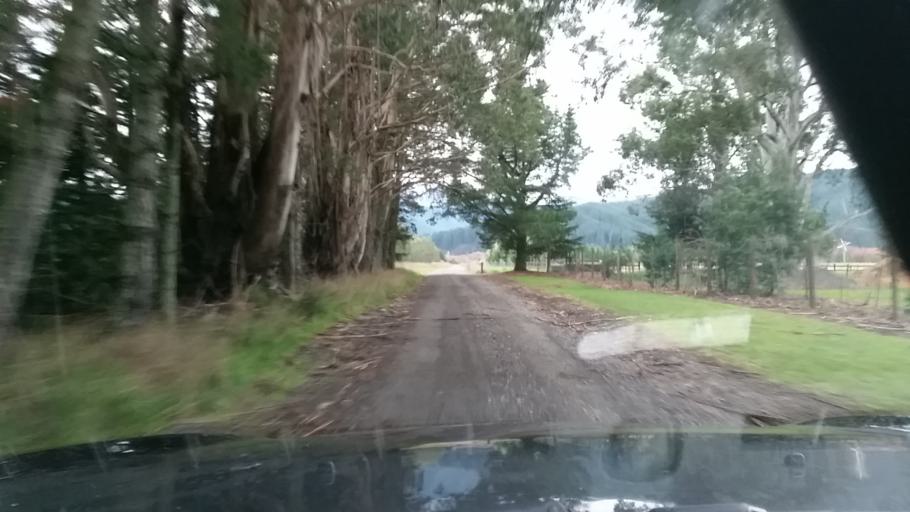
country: NZ
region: Marlborough
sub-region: Marlborough District
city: Blenheim
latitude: -41.5362
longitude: 173.6140
